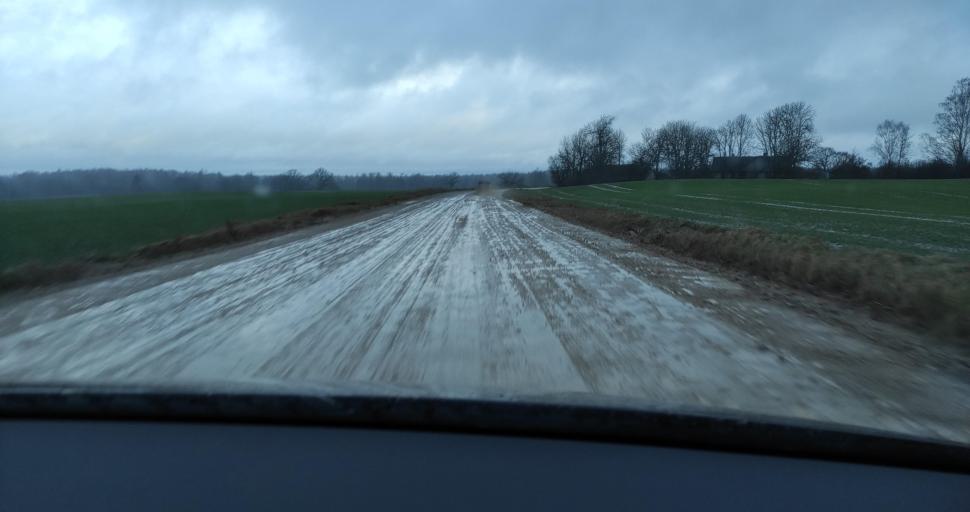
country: LV
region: Skrunda
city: Skrunda
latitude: 56.6989
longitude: 22.2123
